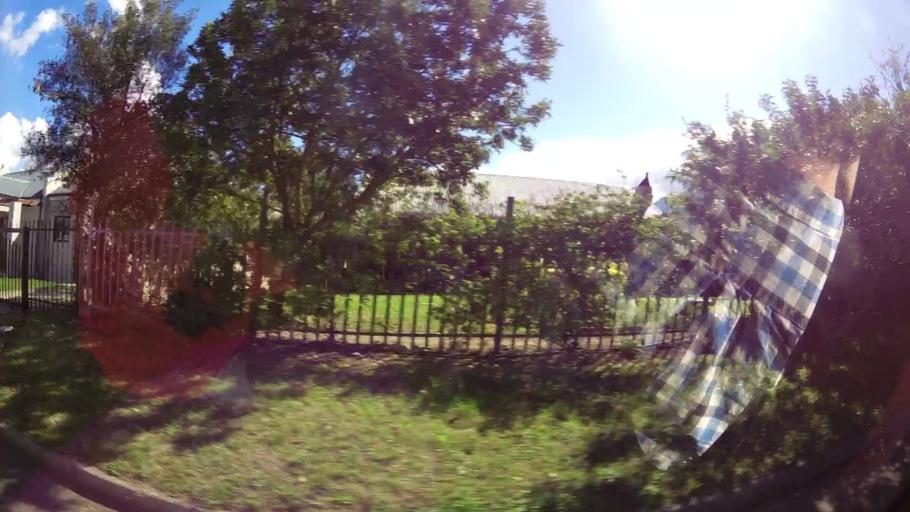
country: ZA
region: Western Cape
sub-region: Overberg District Municipality
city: Swellendam
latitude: -34.0281
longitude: 20.4363
